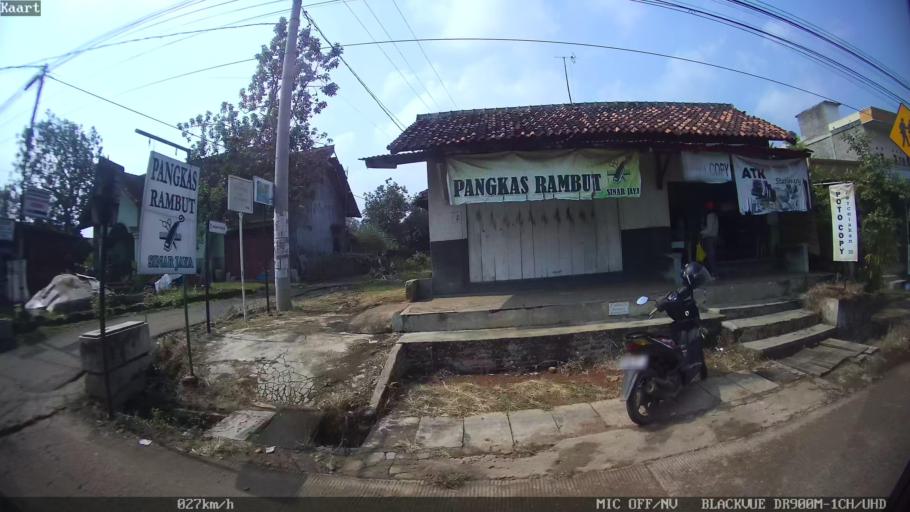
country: ID
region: Lampung
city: Gedongtataan
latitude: -5.3796
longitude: 105.1101
